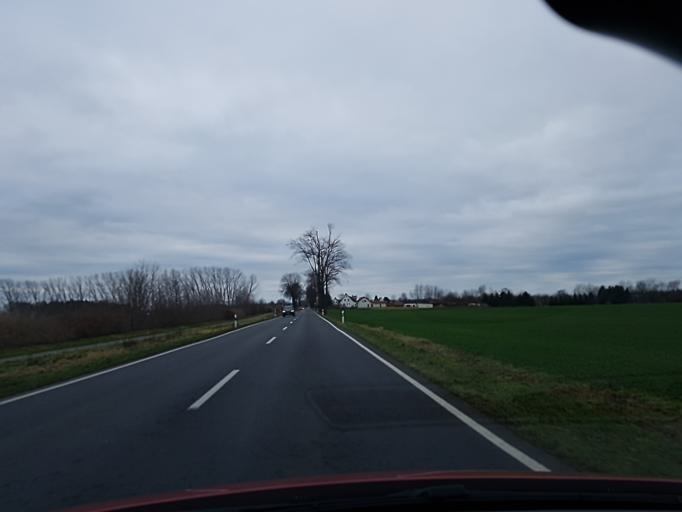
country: DE
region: Brandenburg
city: Elsterwerda
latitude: 51.4354
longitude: 13.5108
